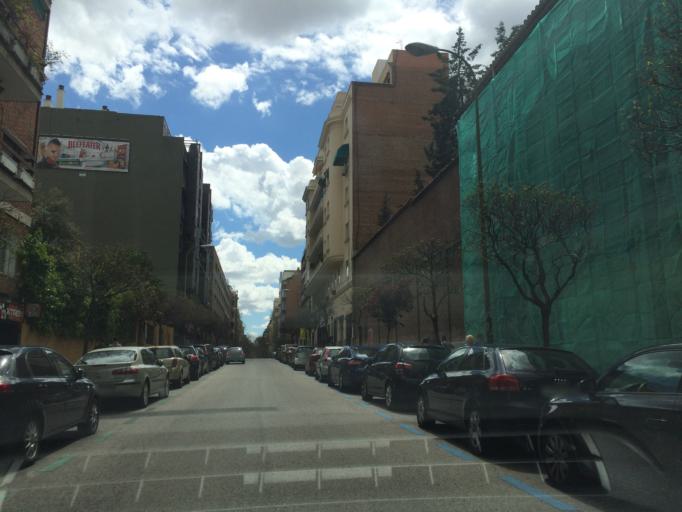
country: ES
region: Madrid
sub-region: Provincia de Madrid
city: Chamberi
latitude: 40.4439
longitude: -3.6989
